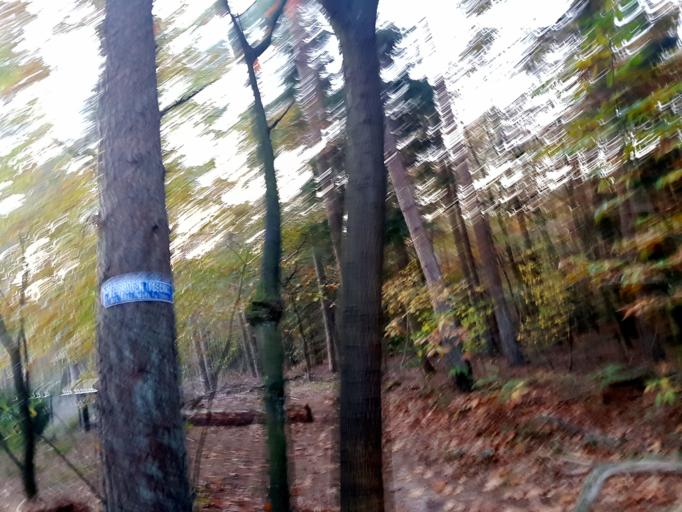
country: NL
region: Gelderland
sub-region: Gemeente Groesbeek
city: Groesbeek
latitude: 51.7849
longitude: 5.8940
